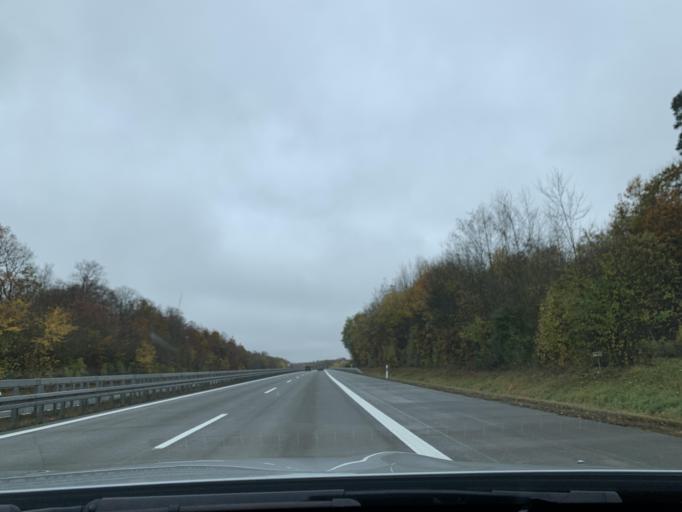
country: DE
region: Baden-Wuerttemberg
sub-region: Regierungsbezirk Stuttgart
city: Buch am Ahorn
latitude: 49.5152
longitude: 9.5683
